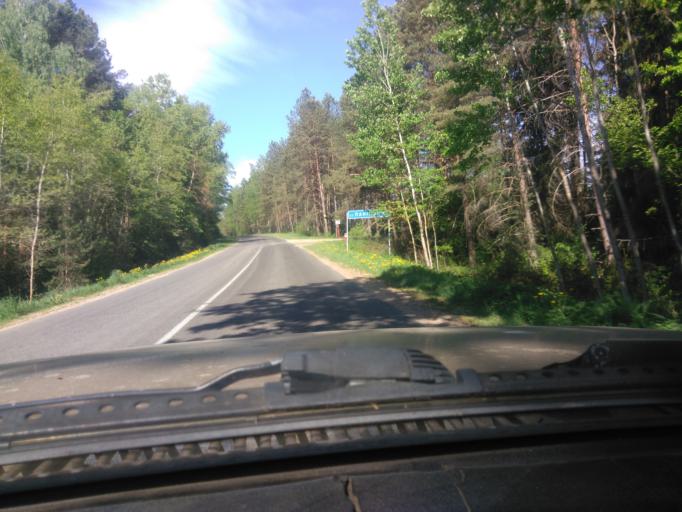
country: BY
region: Mogilev
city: Myazhysyatki
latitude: 53.8134
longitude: 30.1032
